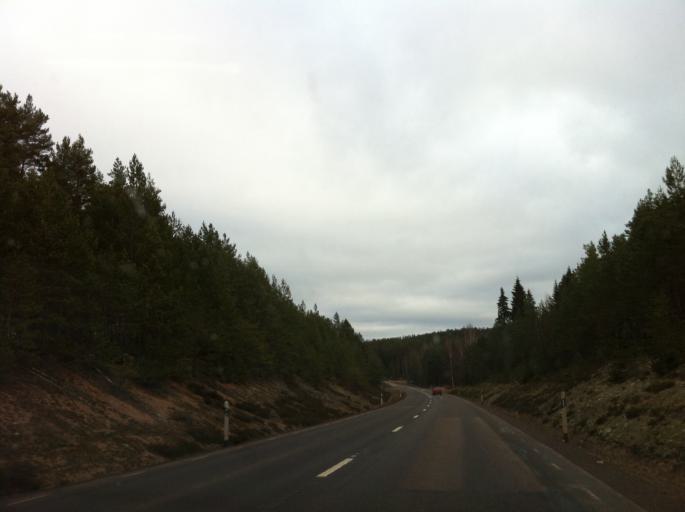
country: SE
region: Kalmar
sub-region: Vimmerby Kommun
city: Vimmerby
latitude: 57.6333
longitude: 15.7399
